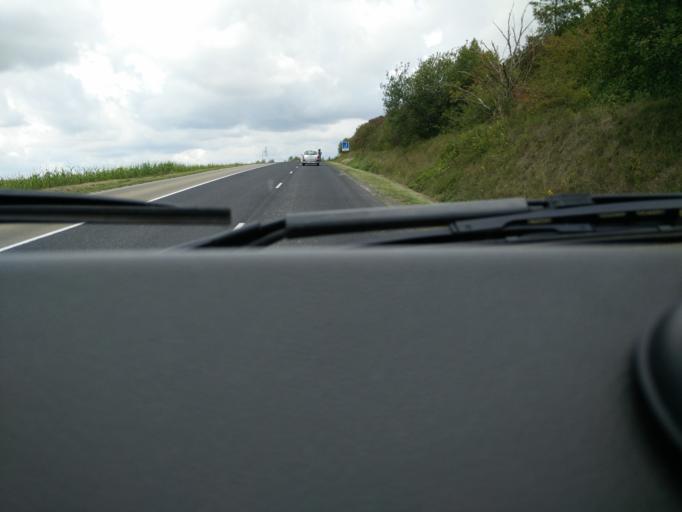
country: FR
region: Lorraine
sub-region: Departement de la Meuse
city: Dugny-sur-Meuse
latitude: 49.1371
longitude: 5.4231
